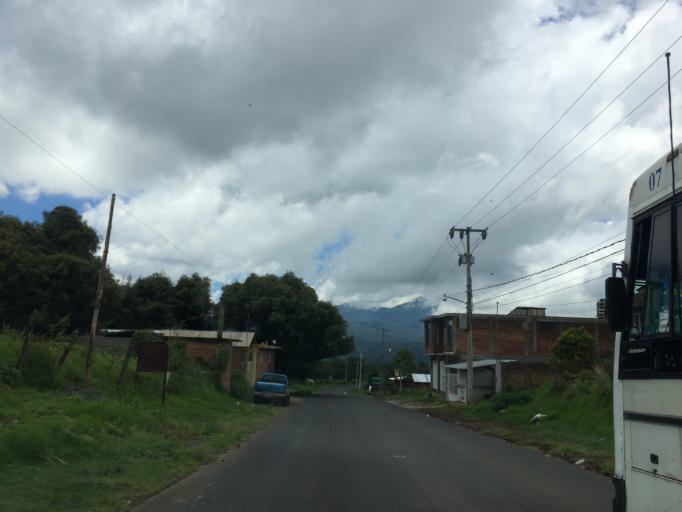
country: MX
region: Michoacan
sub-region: Uruapan
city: Santa Ana Zirosto
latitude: 19.5628
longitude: -102.2908
